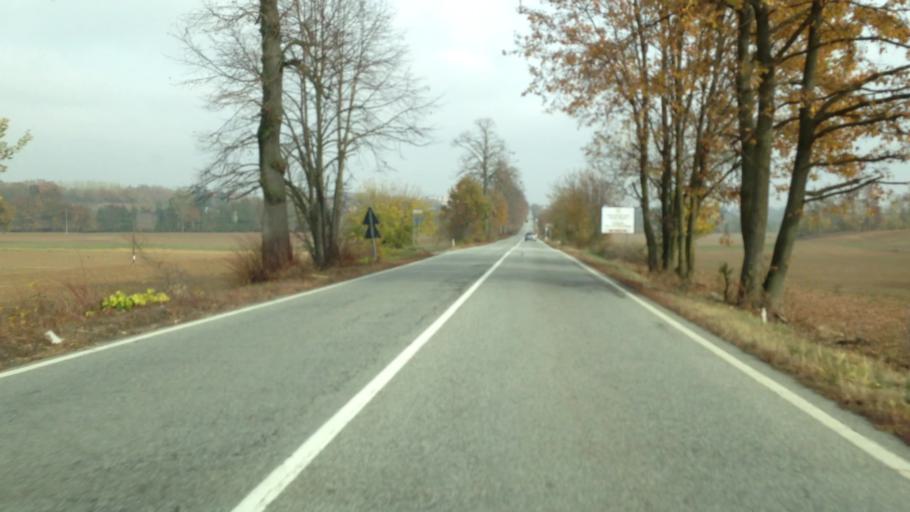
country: IT
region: Piedmont
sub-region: Provincia di Asti
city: Cerro Tanaro
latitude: 44.8907
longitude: 8.3773
